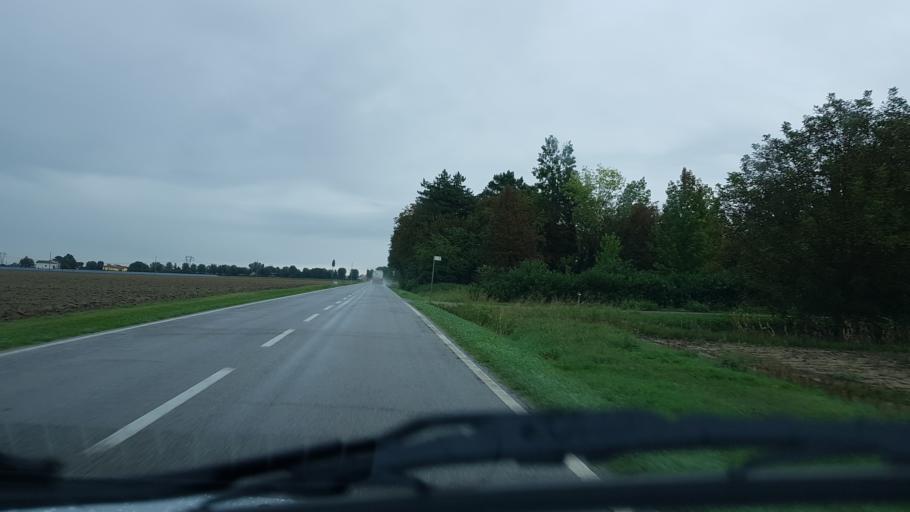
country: IT
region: Emilia-Romagna
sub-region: Provincia di Modena
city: Camposanto
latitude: 44.8031
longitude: 11.1893
